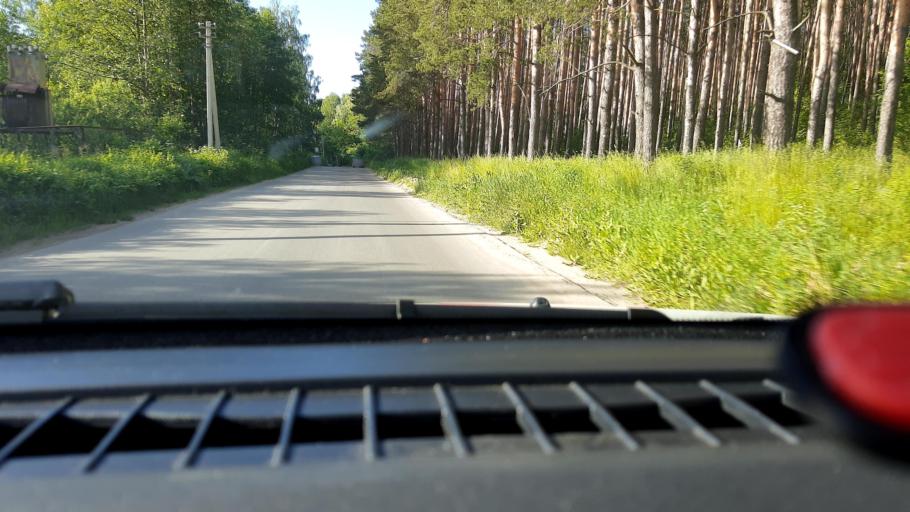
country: RU
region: Nizjnij Novgorod
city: Gorbatovka
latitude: 56.2291
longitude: 43.7628
